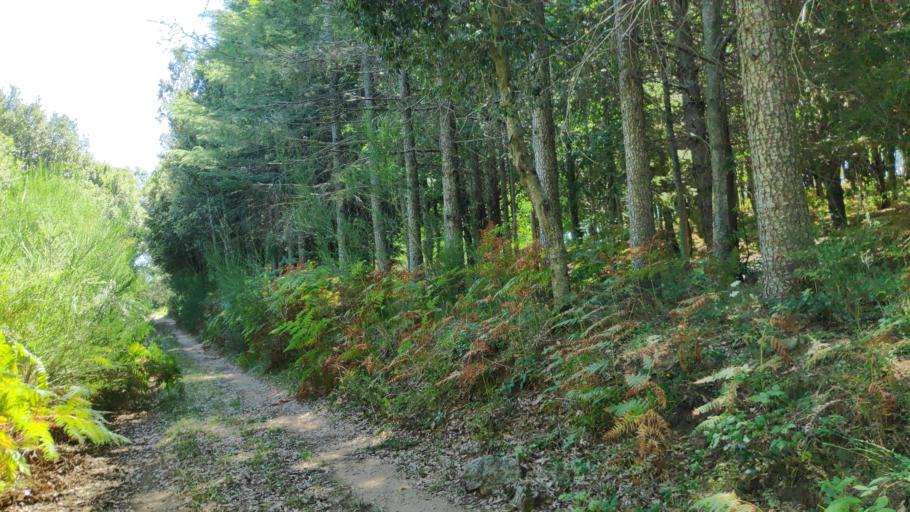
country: IT
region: Calabria
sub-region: Provincia di Vibo-Valentia
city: Nardodipace
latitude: 38.4786
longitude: 16.3902
